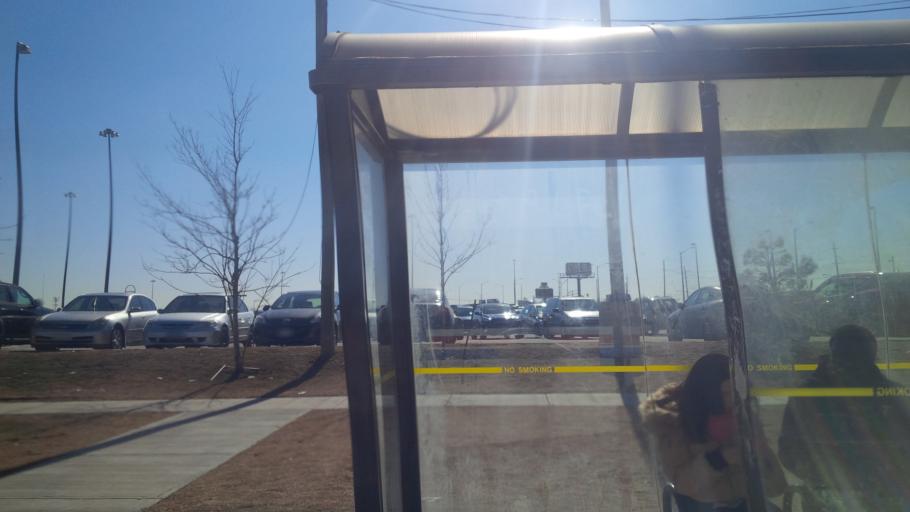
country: CA
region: Ontario
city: Brampton
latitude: 43.7042
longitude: -79.6898
